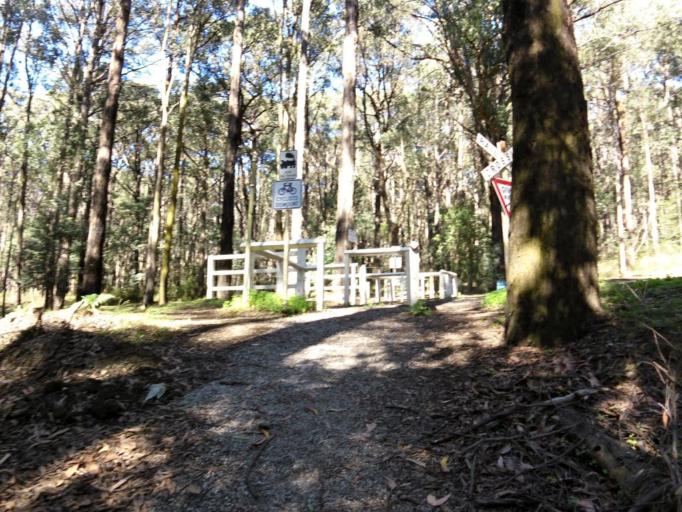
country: AU
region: Victoria
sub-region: Cardinia
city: Cockatoo
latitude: -37.9290
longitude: 145.4699
